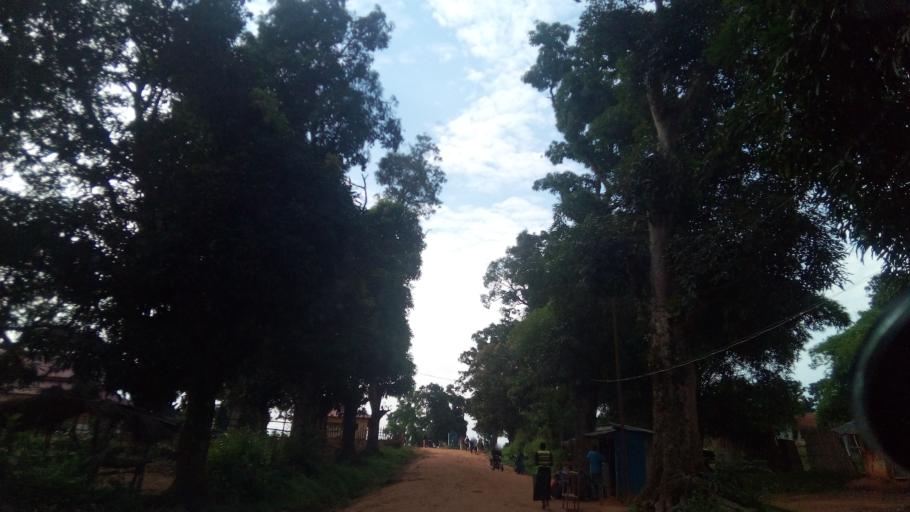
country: CD
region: Kasai-Oriental
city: Kabinda
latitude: -6.1326
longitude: 24.4848
